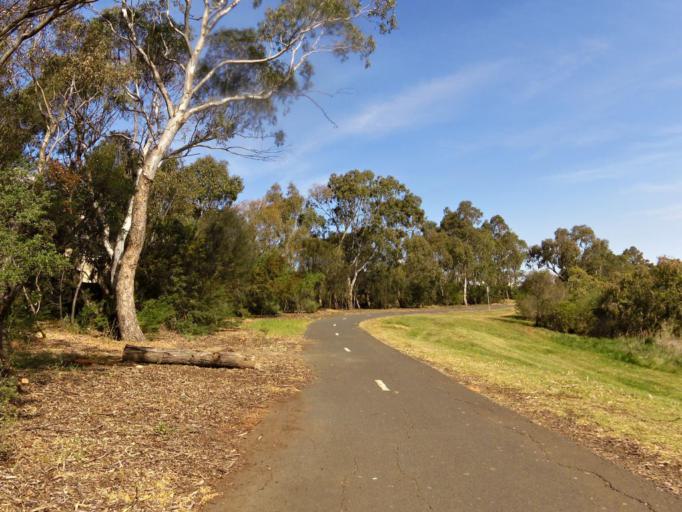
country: AU
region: Victoria
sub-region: Brimbank
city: Sunshine West
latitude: -37.7750
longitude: 144.8082
